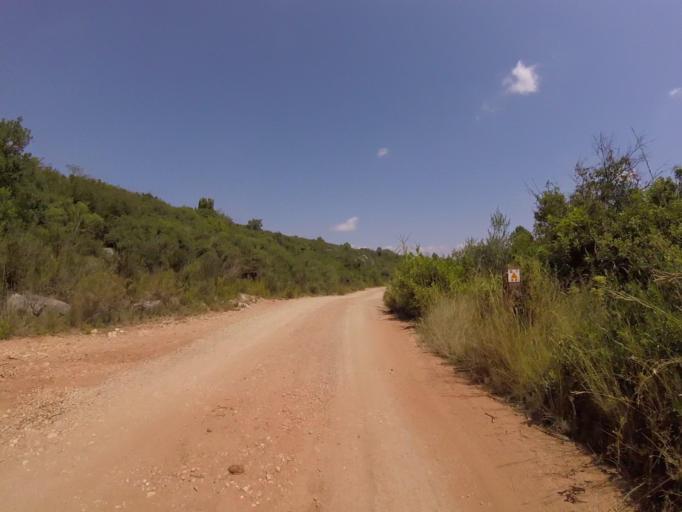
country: ES
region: Valencia
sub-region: Provincia de Castello
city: Torreblanca
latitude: 40.2252
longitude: 0.1551
